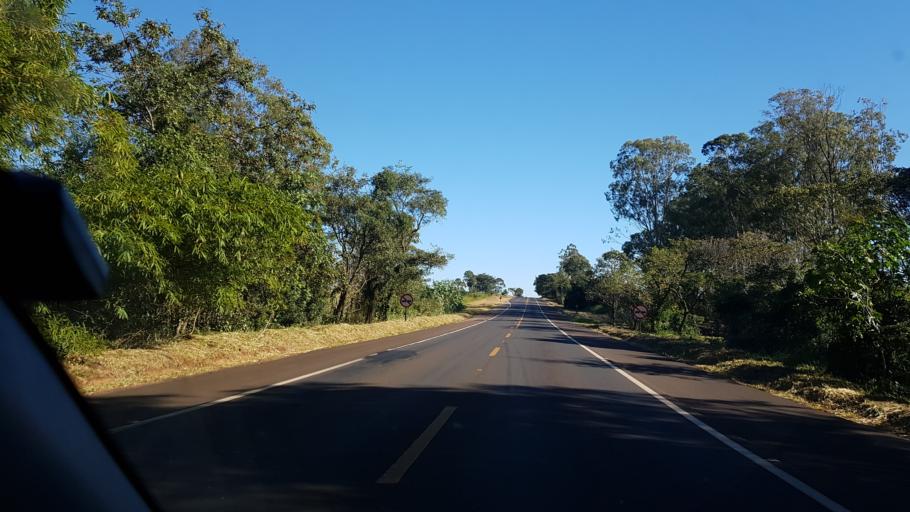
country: BR
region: Sao Paulo
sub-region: Assis
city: Assis
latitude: -22.5799
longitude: -50.5073
